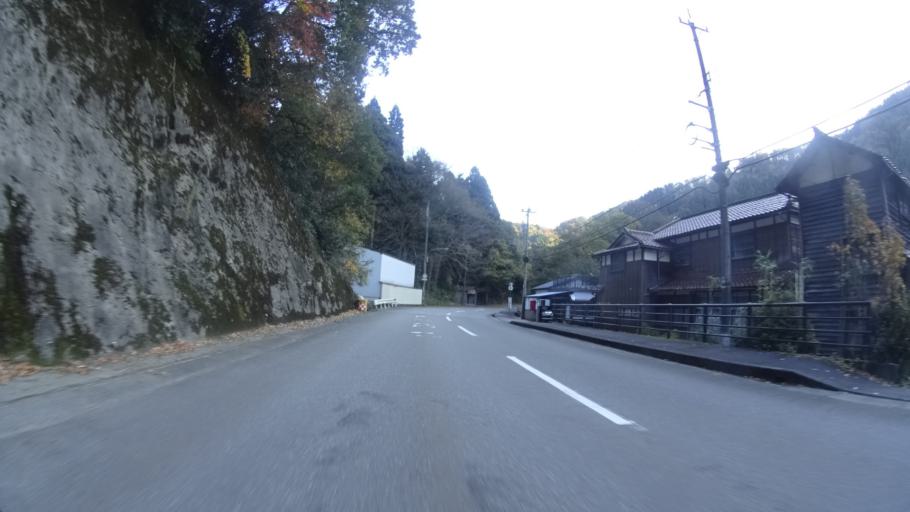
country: JP
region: Fukui
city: Maruoka
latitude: 36.2240
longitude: 136.3589
